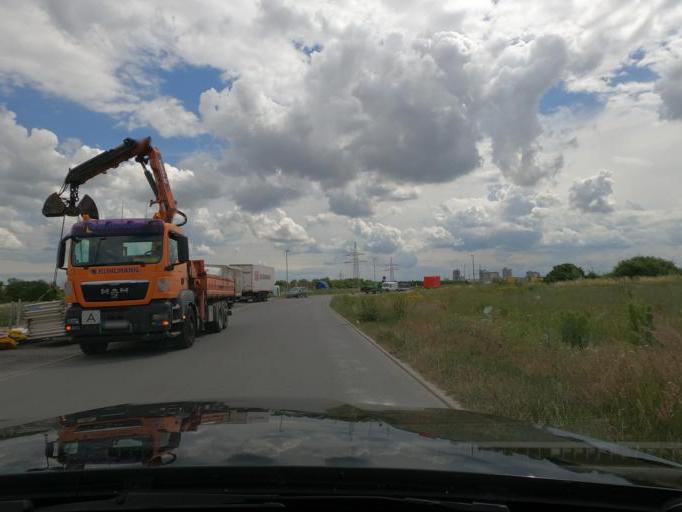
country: DE
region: Lower Saxony
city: Laatzen
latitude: 52.3667
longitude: 9.8707
